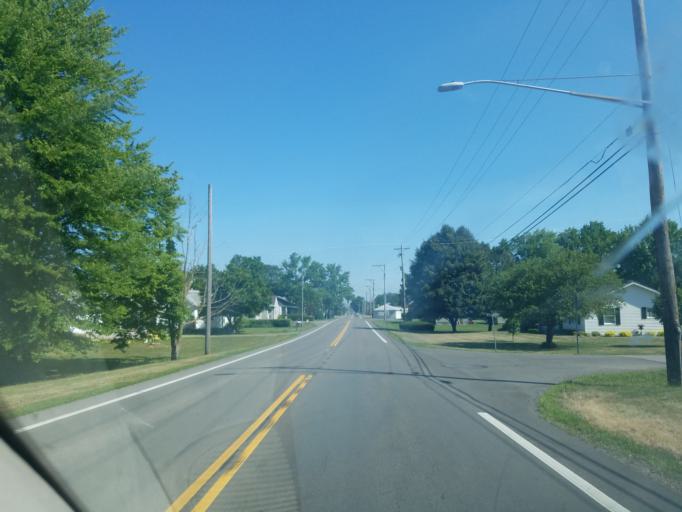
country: US
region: Ohio
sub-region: Logan County
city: Northwood
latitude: 40.4379
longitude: -83.8051
